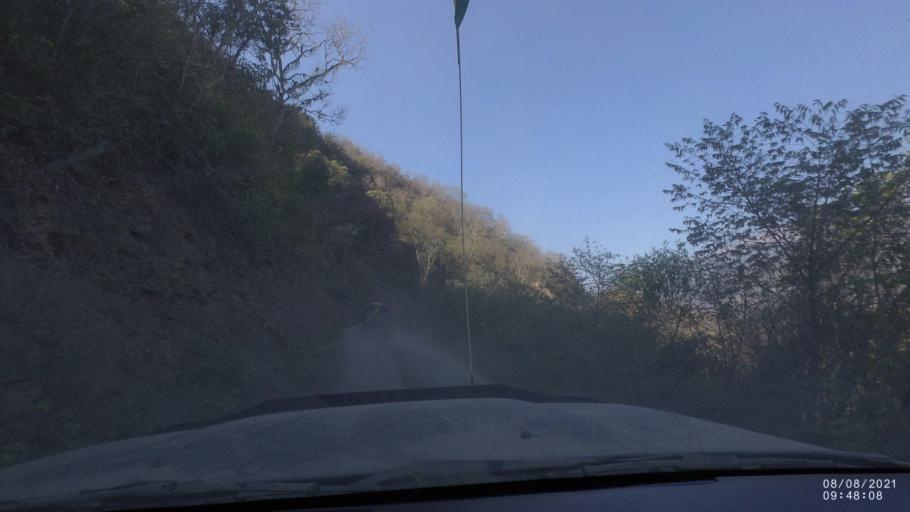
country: BO
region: La Paz
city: Quime
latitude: -16.6115
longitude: -66.7288
